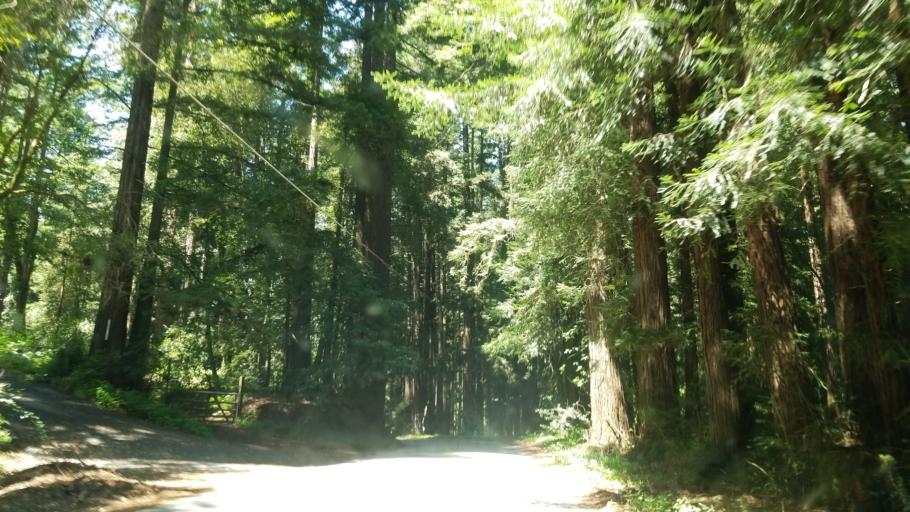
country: US
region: California
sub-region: Santa Cruz County
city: Amesti
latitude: 37.0118
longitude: -121.7515
